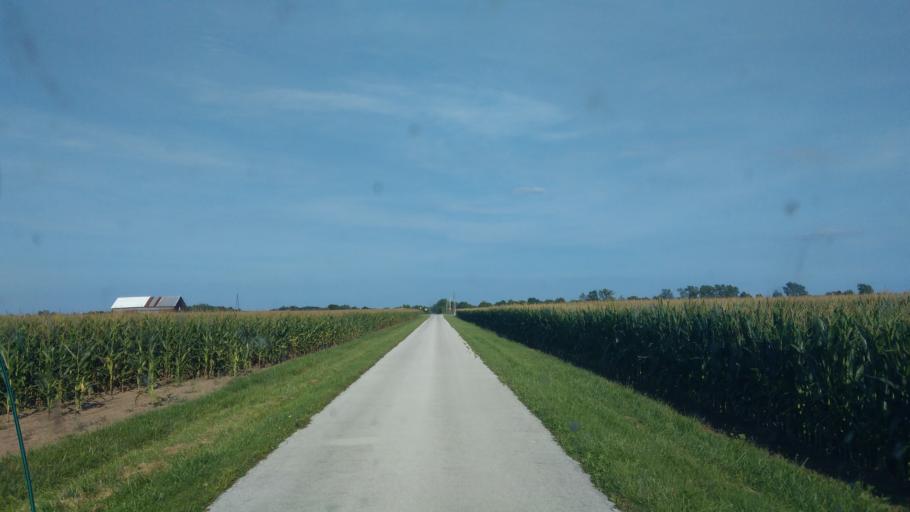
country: US
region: Ohio
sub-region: Wyandot County
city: Carey
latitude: 40.8466
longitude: -83.4026
